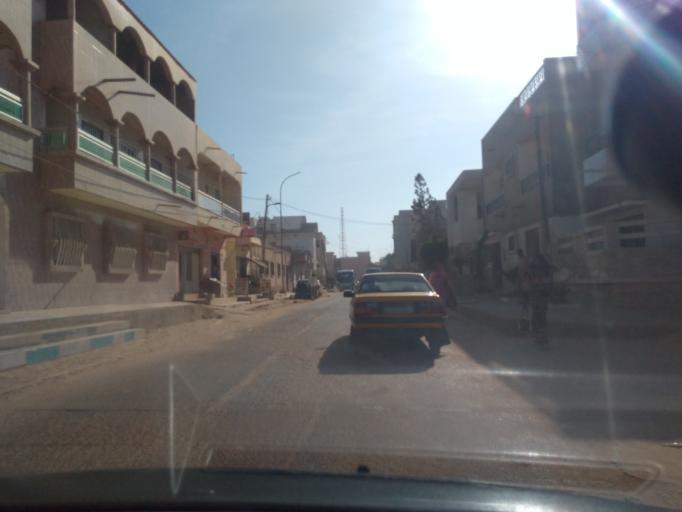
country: SN
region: Dakar
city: Grand Dakar
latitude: 14.7629
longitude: -17.4468
